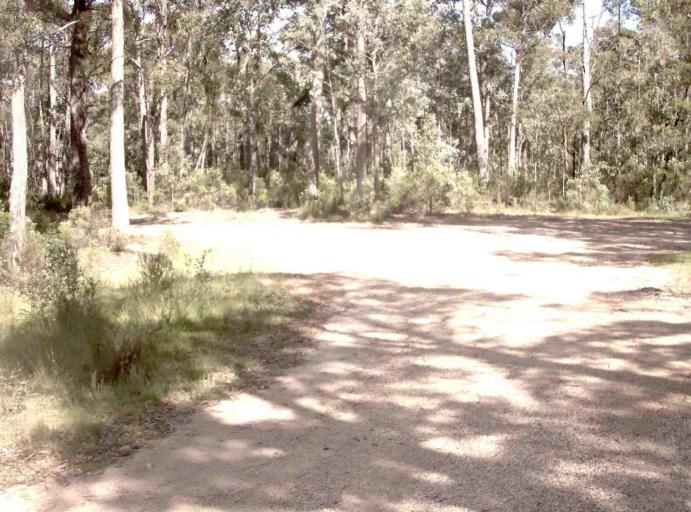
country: AU
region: Victoria
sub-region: East Gippsland
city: Lakes Entrance
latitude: -37.4729
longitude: 148.1242
